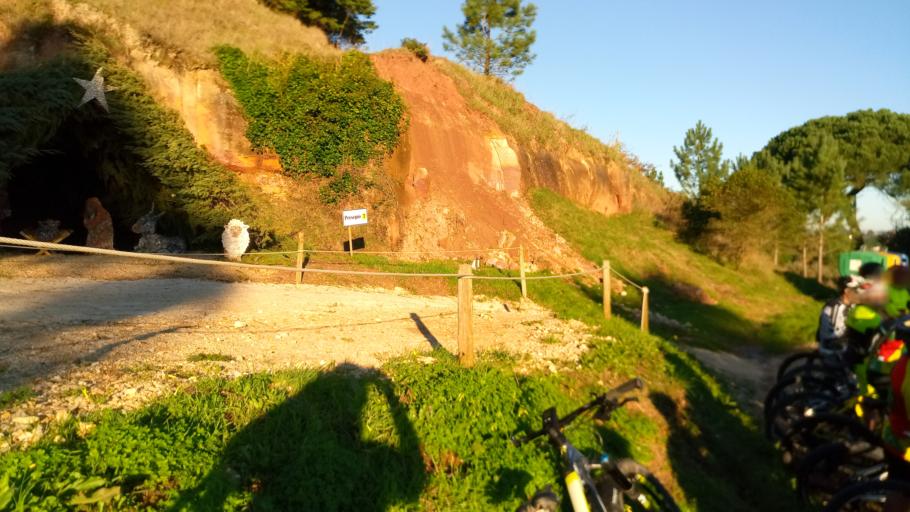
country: PT
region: Leiria
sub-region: Caldas da Rainha
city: Caldas da Rainha
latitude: 39.3829
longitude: -9.0735
